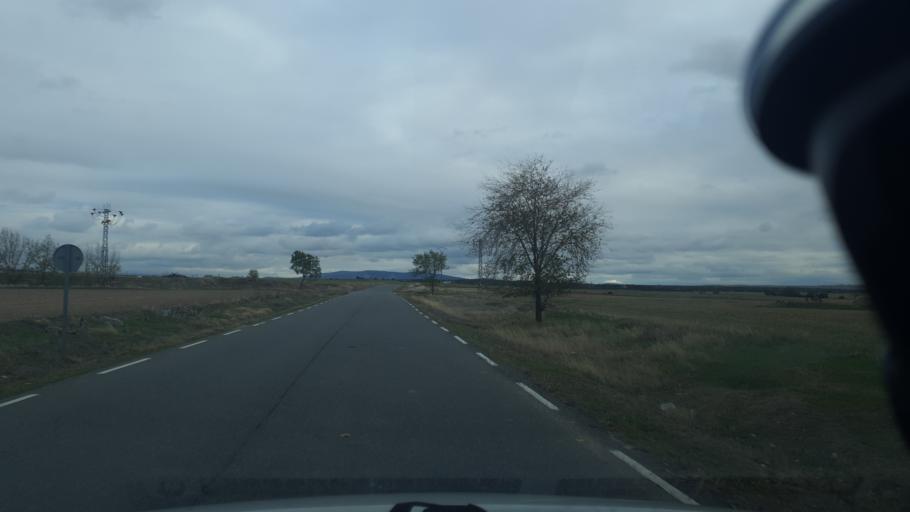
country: ES
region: Castille and Leon
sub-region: Provincia de Avila
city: Velayos
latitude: 40.8383
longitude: -4.6199
